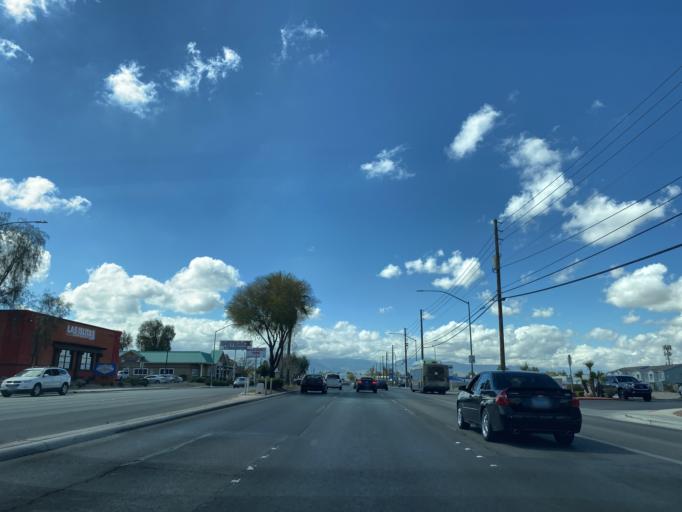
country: US
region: Nevada
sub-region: Clark County
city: North Las Vegas
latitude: 36.2395
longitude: -115.1761
